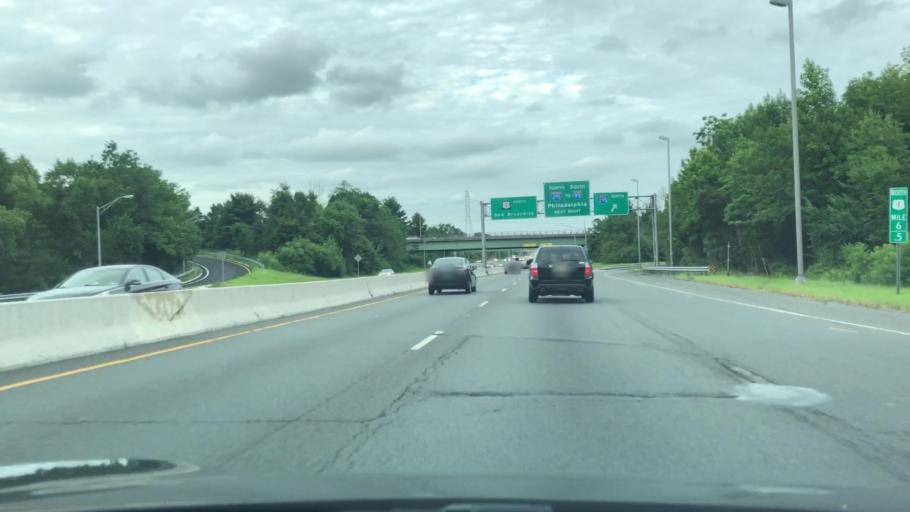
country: US
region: New Jersey
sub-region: Mercer County
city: Lawrenceville
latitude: 40.2809
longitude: -74.6991
